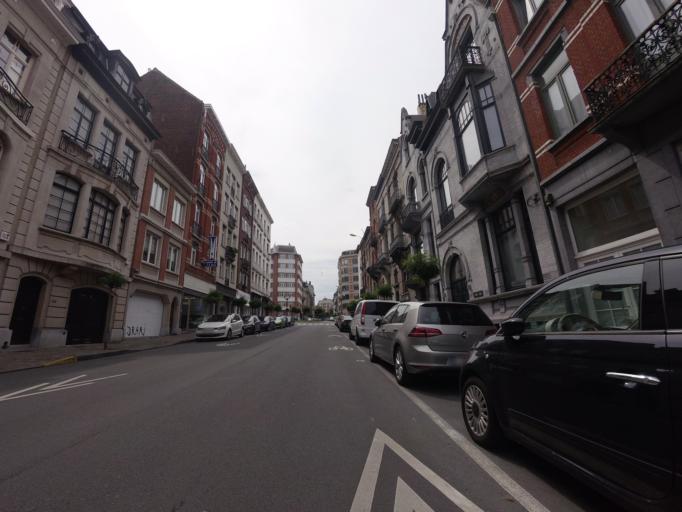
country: BE
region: Brussels Capital
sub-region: Bruxelles-Capitale
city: Brussels
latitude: 50.8209
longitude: 4.3630
